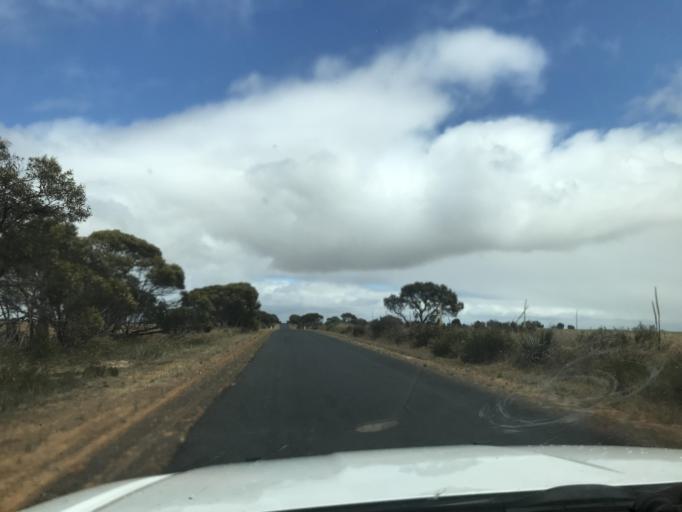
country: AU
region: South Australia
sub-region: Tatiara
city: Bordertown
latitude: -36.1370
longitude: 141.1984
